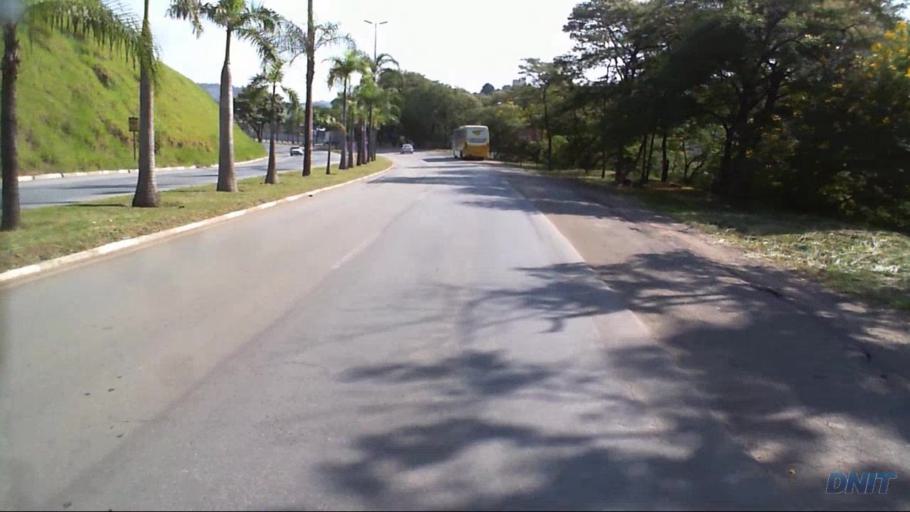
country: BR
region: Minas Gerais
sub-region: Ipatinga
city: Ipatinga
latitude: -19.4620
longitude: -42.5316
